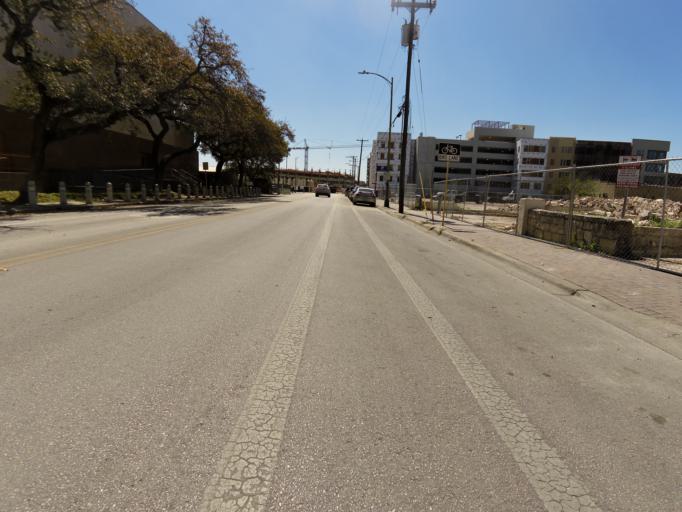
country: US
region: Texas
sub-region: Bexar County
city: San Antonio
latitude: 29.4223
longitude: -98.4943
